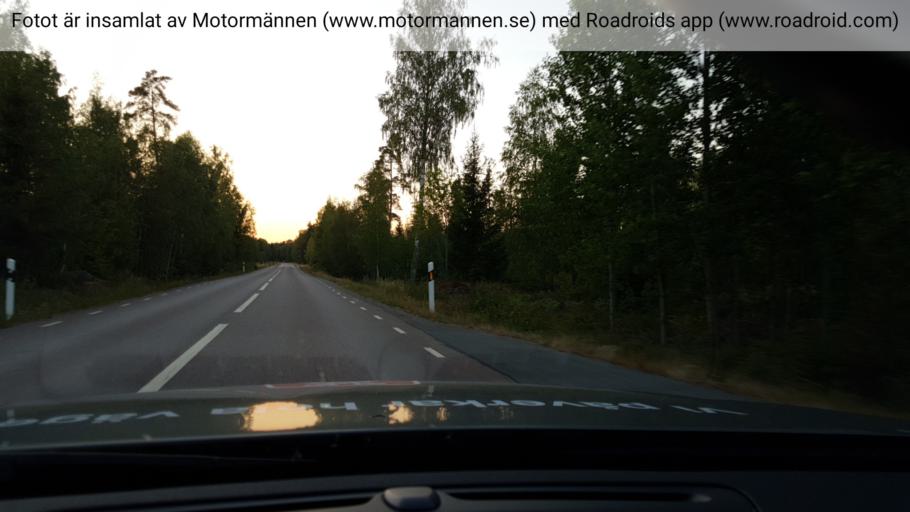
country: SE
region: Uppsala
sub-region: Heby Kommun
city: OEstervala
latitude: 60.0231
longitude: 17.2822
